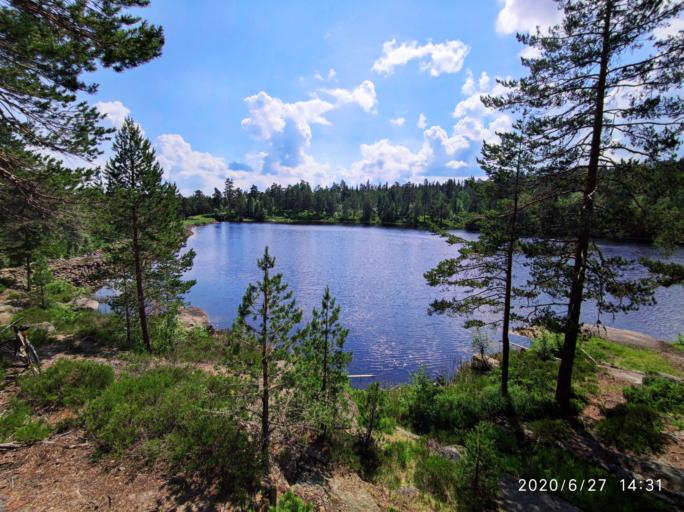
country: NO
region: Buskerud
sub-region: Kongsberg
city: Kongsberg
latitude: 59.6646
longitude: 9.5872
